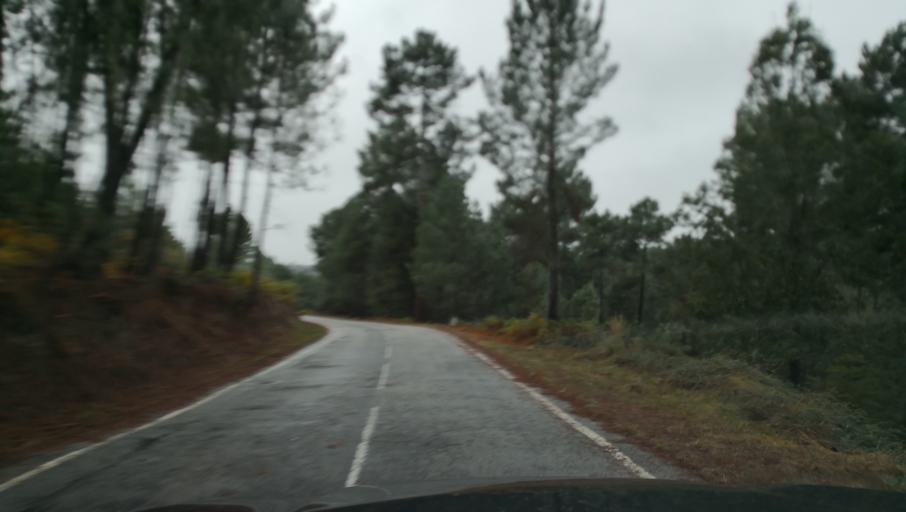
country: PT
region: Vila Real
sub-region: Sabrosa
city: Sabrosa
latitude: 41.3495
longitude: -7.5864
